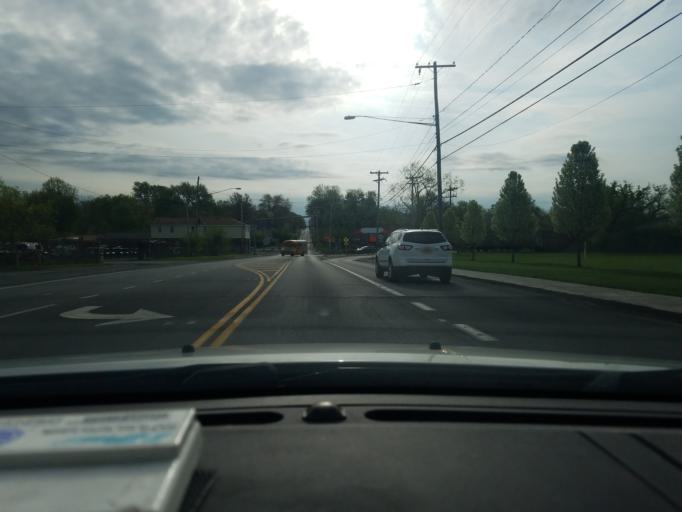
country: US
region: New York
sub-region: Onondaga County
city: East Syracuse
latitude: 43.0698
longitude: -76.0874
